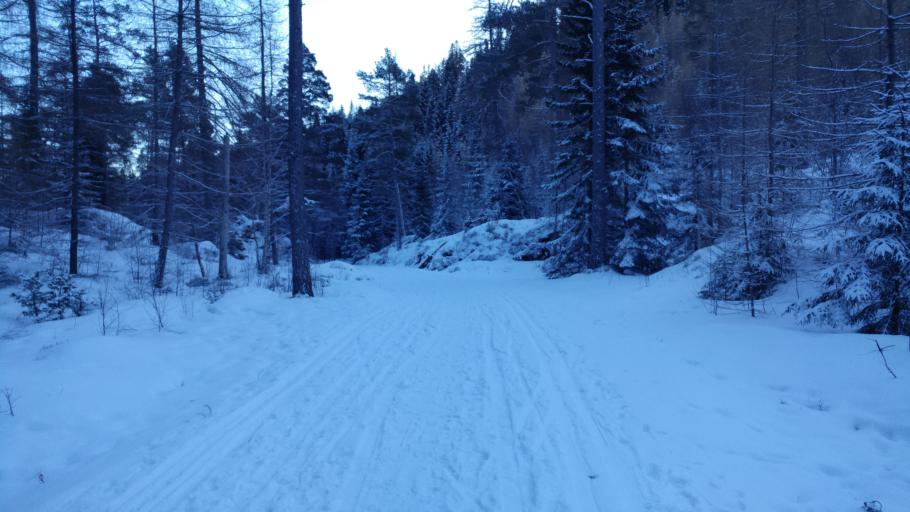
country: NO
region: Sor-Trondelag
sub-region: Trondheim
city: Trondheim
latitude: 63.4391
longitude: 10.3368
